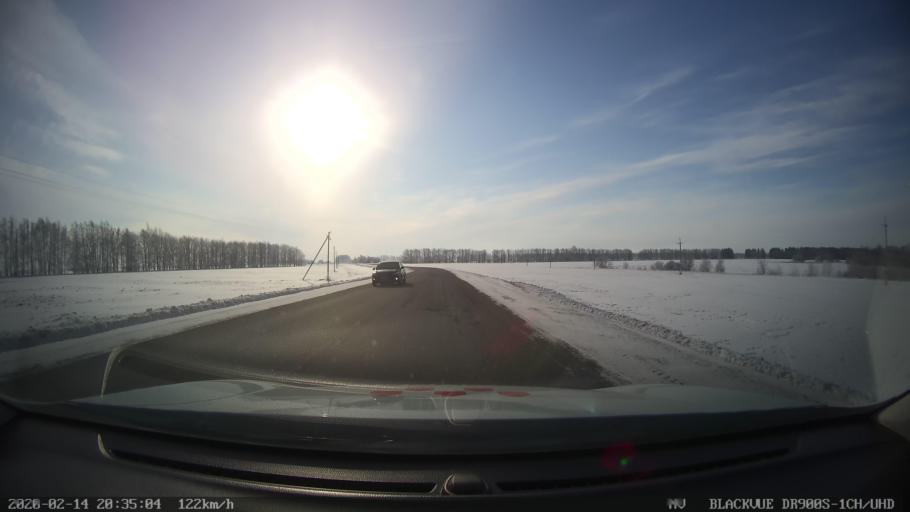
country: RU
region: Tatarstan
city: Kuybyshevskiy Zaton
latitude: 55.3882
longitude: 48.9800
